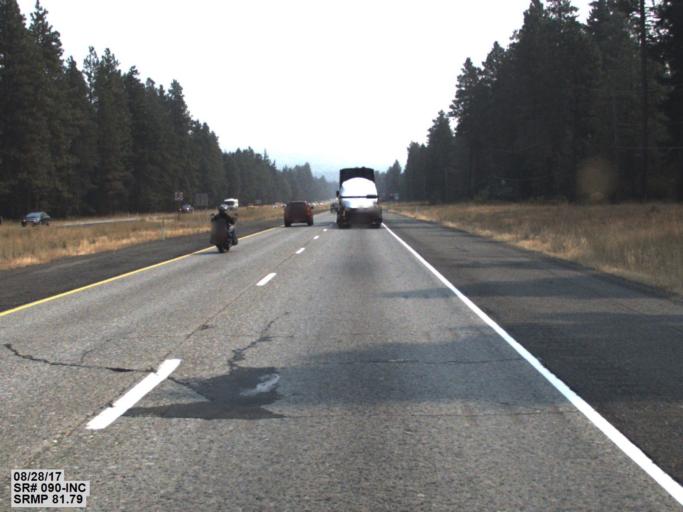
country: US
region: Washington
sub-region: Kittitas County
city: Cle Elum
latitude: 47.1879
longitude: -120.9845
